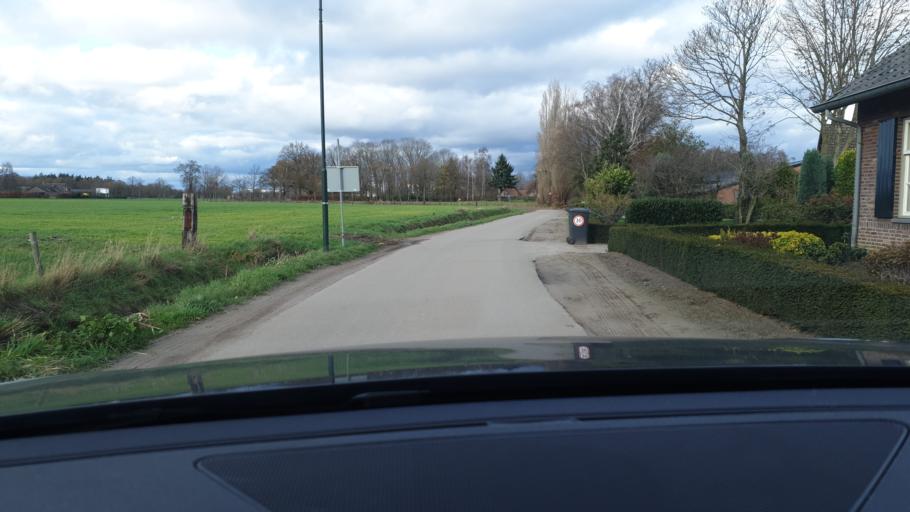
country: NL
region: North Brabant
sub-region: Gemeente Waalre
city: Waalre
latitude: 51.3793
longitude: 5.4330
